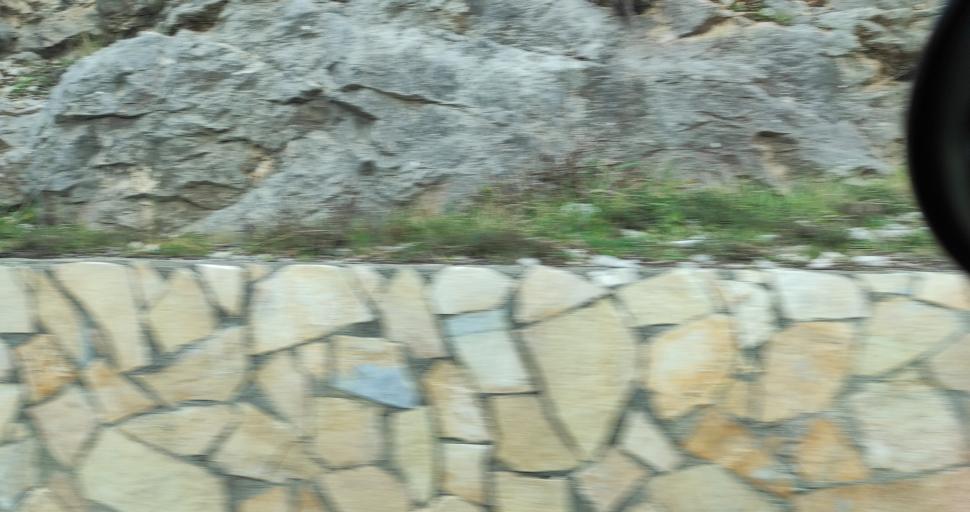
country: AL
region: Lezhe
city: Shengjin
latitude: 41.8023
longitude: 19.6154
